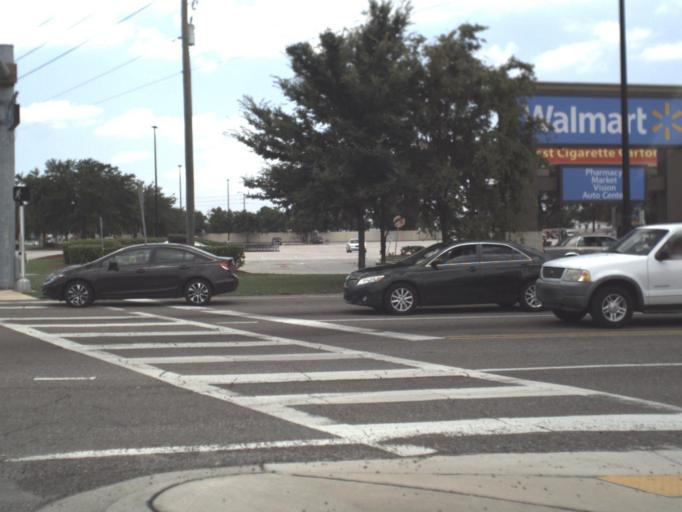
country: US
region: Florida
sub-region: Pinellas County
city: Pinellas Park
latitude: 27.8446
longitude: -82.6874
